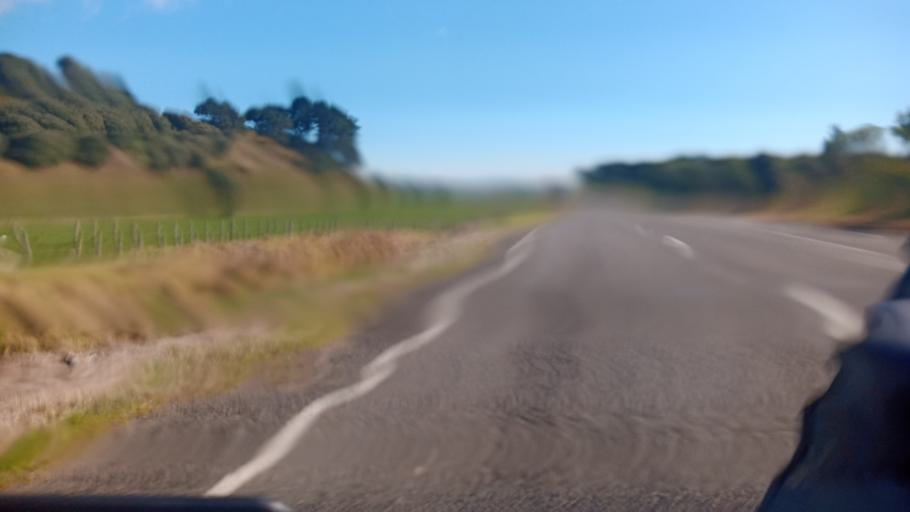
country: NZ
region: Bay of Plenty
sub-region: Opotiki District
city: Opotiki
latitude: -37.9909
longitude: 177.3114
